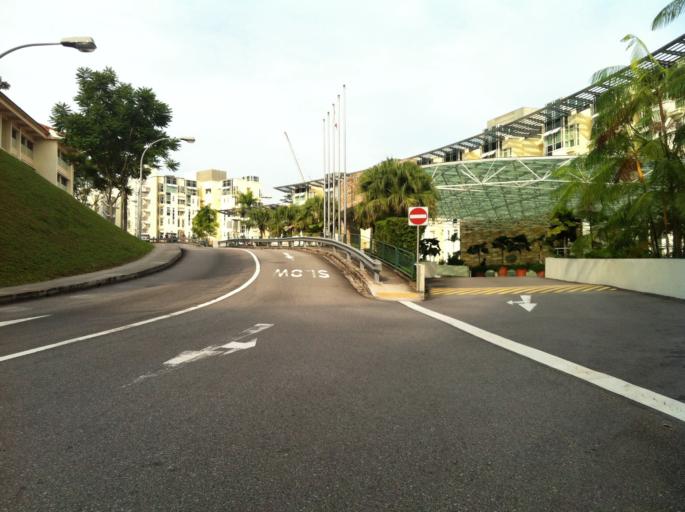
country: SG
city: Singapore
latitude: 1.2913
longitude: 103.7808
